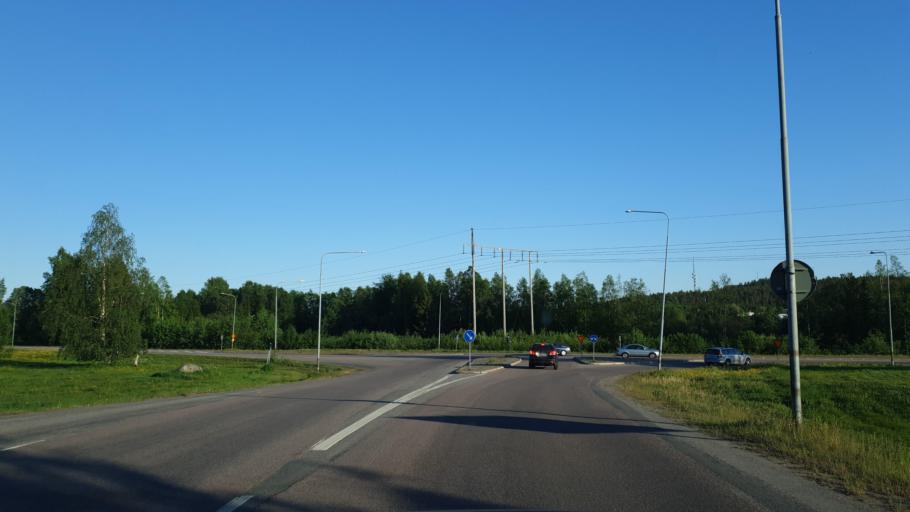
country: SE
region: Norrbotten
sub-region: Lulea Kommun
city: Lulea
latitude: 65.6158
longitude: 22.1482
